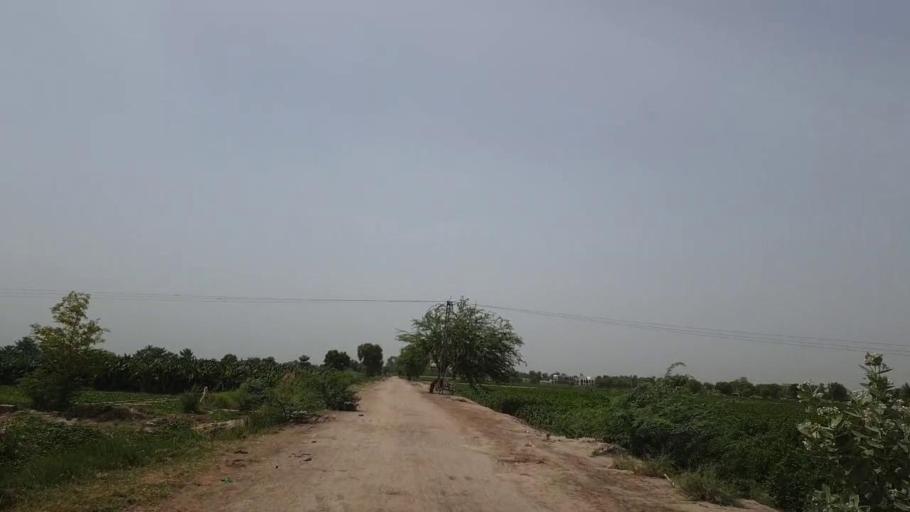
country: PK
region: Sindh
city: Sakrand
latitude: 26.1326
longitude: 68.2865
